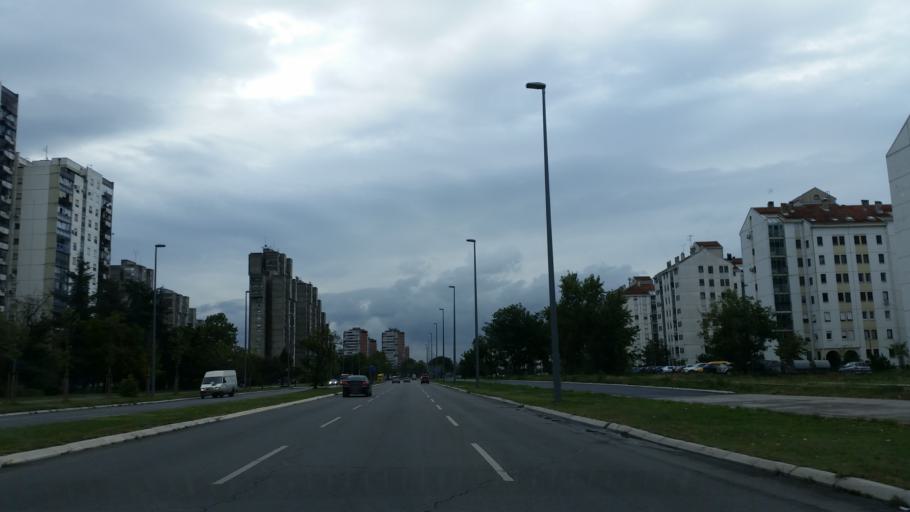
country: RS
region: Central Serbia
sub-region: Belgrade
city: Zemun
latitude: 44.8026
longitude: 20.3672
